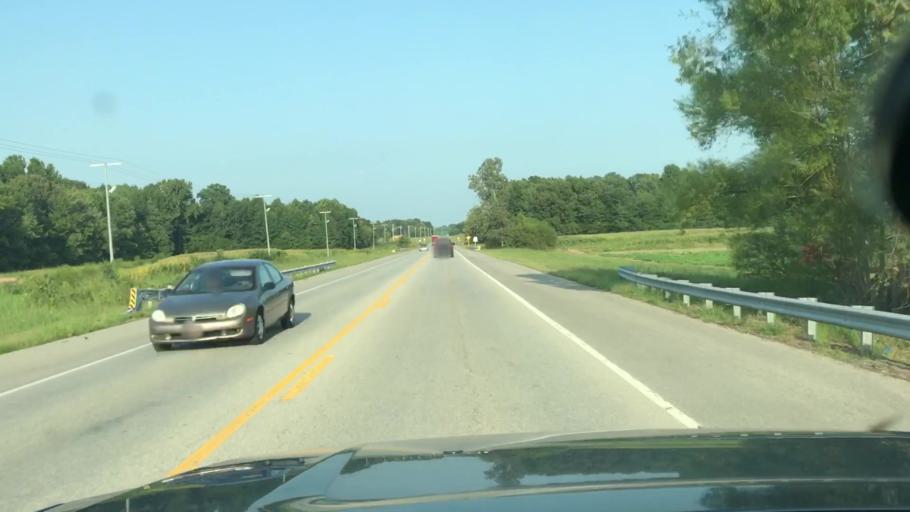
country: US
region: Tennessee
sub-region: Sumner County
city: Portland
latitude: 36.5794
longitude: -86.5541
